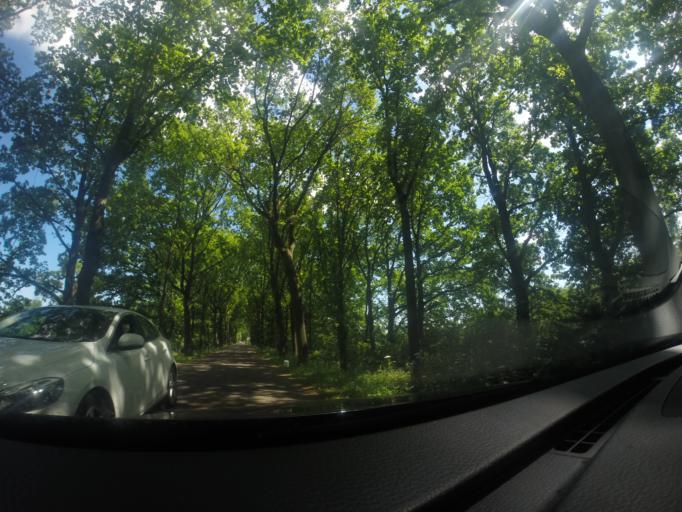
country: NL
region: Gelderland
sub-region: Gemeente Renkum
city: Doorwerth
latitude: 51.9677
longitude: 5.7849
